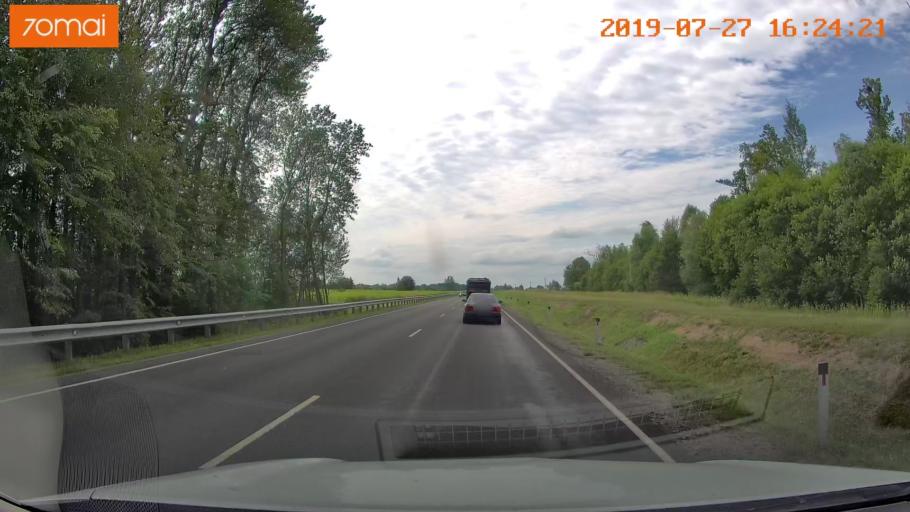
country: RU
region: Kaliningrad
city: Zheleznodorozhnyy
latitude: 54.6339
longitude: 21.4544
